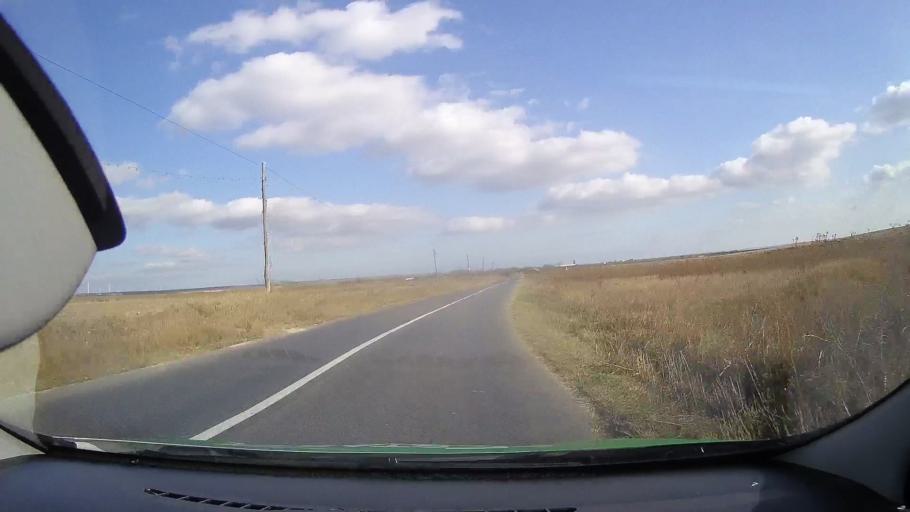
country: RO
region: Constanta
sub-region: Comuna Cogealac
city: Cogealac
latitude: 44.5610
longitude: 28.5765
